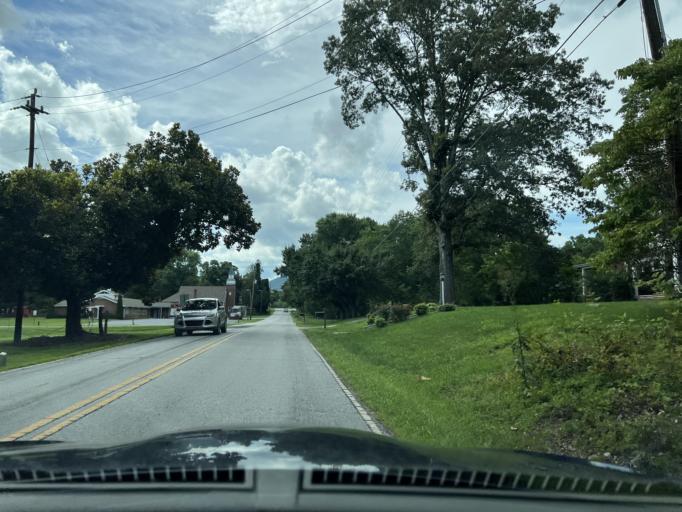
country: US
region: North Carolina
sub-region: Henderson County
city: Fruitland
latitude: 35.3951
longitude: -82.3907
